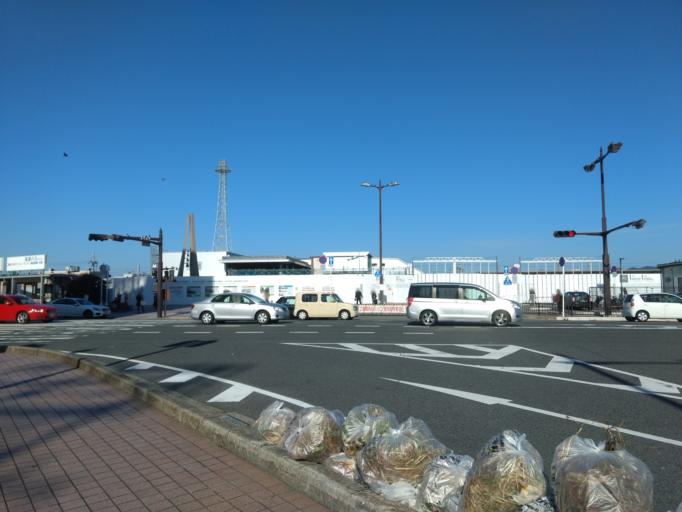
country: JP
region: Wakayama
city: Wakayama-shi
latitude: 34.2360
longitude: 135.1677
